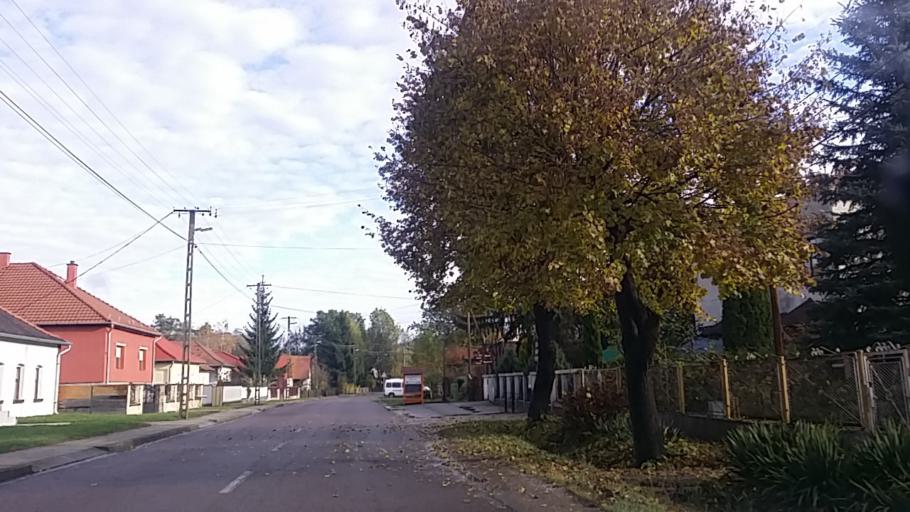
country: HU
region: Heves
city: Szilvasvarad
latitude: 48.1701
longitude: 20.4861
